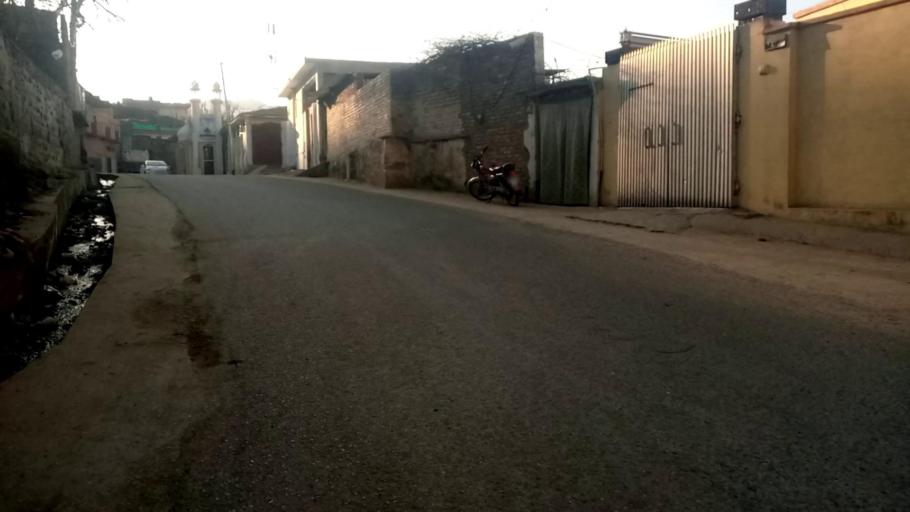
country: PK
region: Khyber Pakhtunkhwa
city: Saidu Sharif
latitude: 34.7431
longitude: 72.3585
